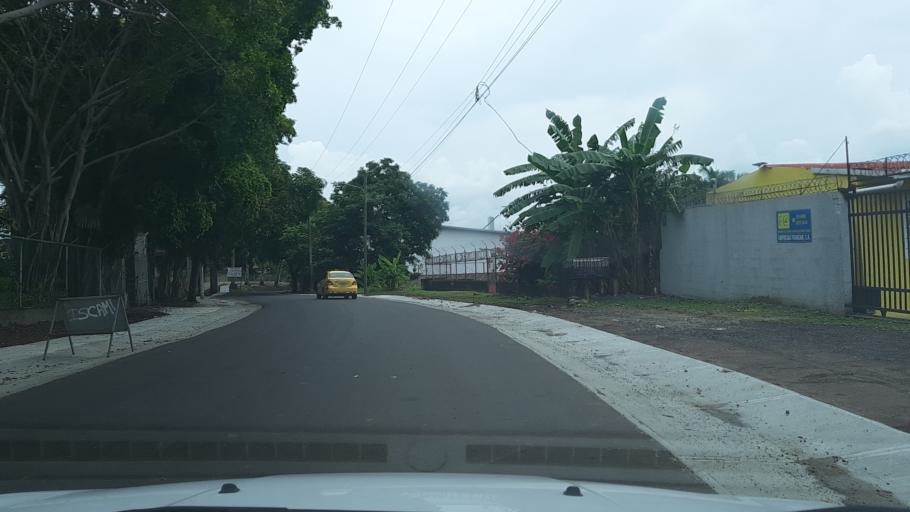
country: PA
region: Panama
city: San Miguelito
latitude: 9.0298
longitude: -79.4811
